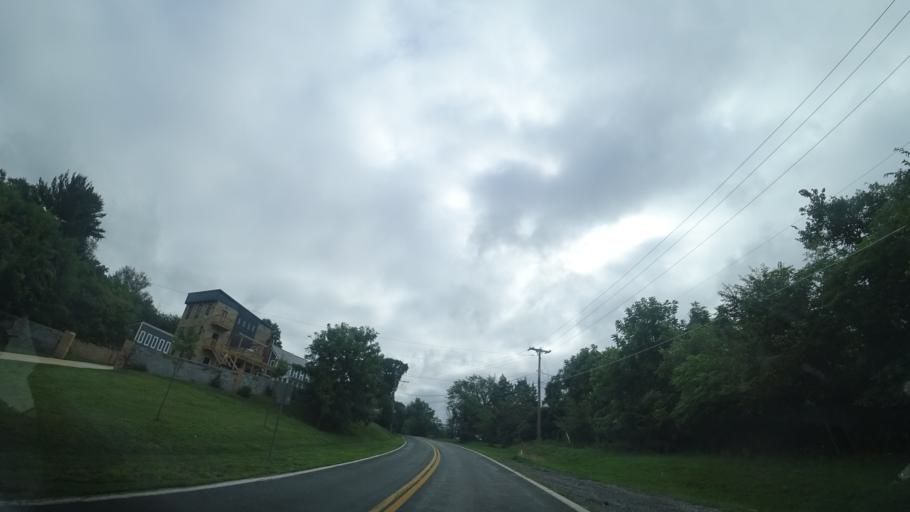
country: US
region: Virginia
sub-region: Loudoun County
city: Lowes Island
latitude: 39.0781
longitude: -77.3327
